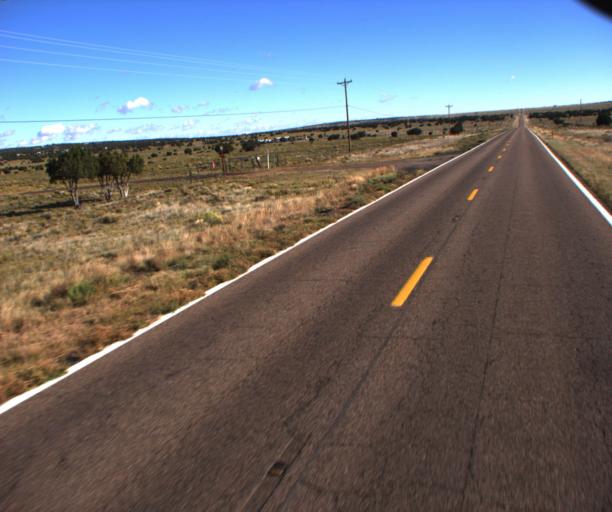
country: US
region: Arizona
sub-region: Navajo County
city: White Mountain Lake
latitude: 34.3428
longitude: -109.7302
